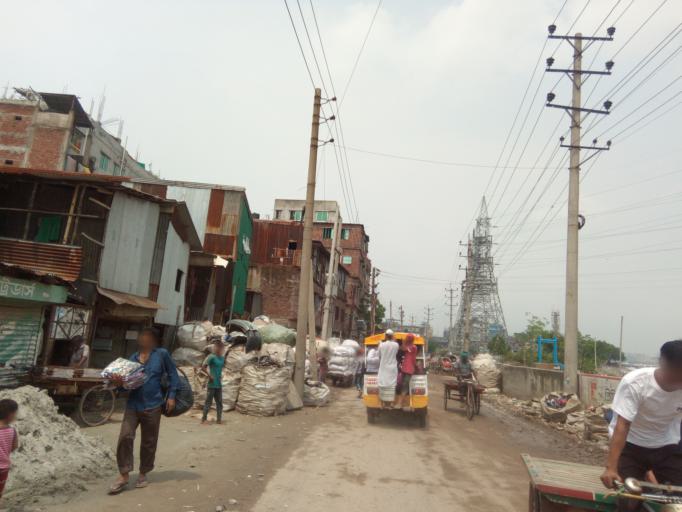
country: BD
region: Dhaka
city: Azimpur
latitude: 23.7121
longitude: 90.3884
